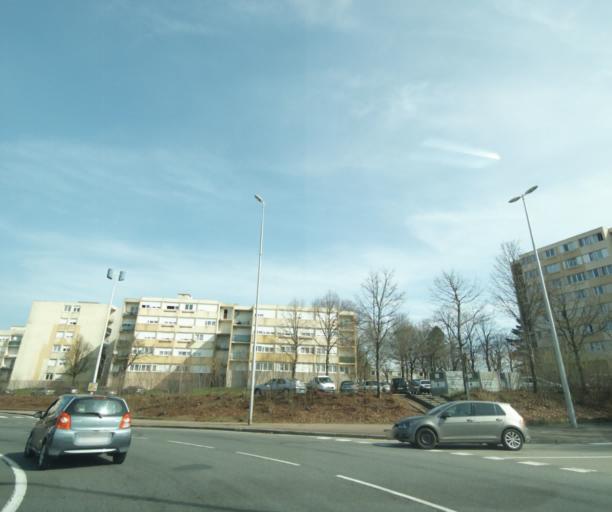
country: FR
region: Limousin
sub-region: Departement de la Haute-Vienne
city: Rilhac-Rancon
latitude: 45.8810
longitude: 1.2948
